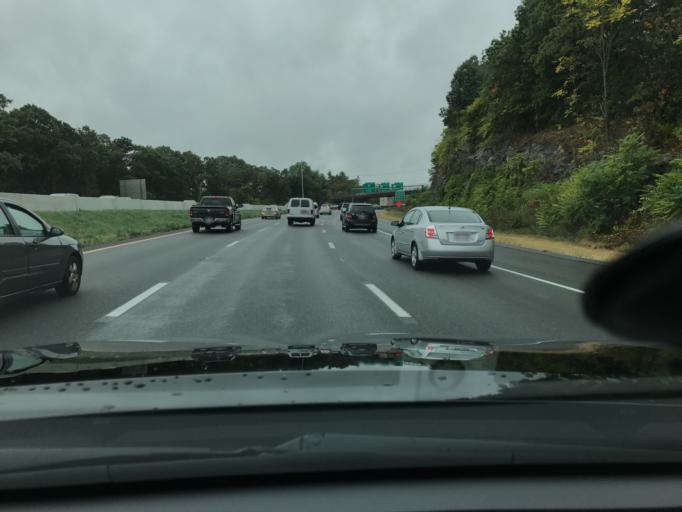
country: US
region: Massachusetts
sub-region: Middlesex County
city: Reading
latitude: 42.5063
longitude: -71.0953
